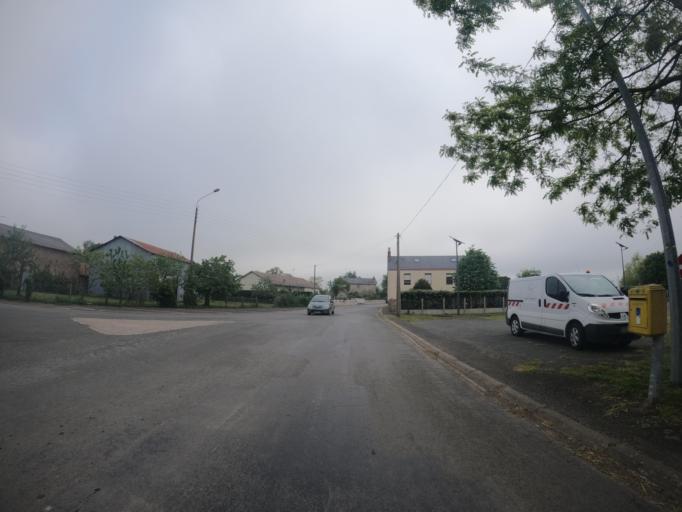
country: FR
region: Poitou-Charentes
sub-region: Departement des Deux-Sevres
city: Mauze-Thouarsais
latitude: 46.8971
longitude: -0.3303
